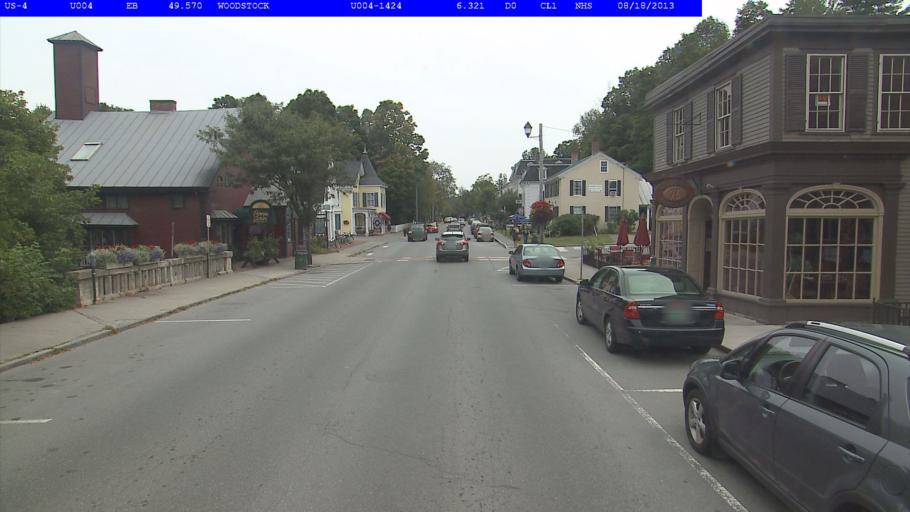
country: US
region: Vermont
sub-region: Windsor County
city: Woodstock
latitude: 43.6255
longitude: -72.5174
